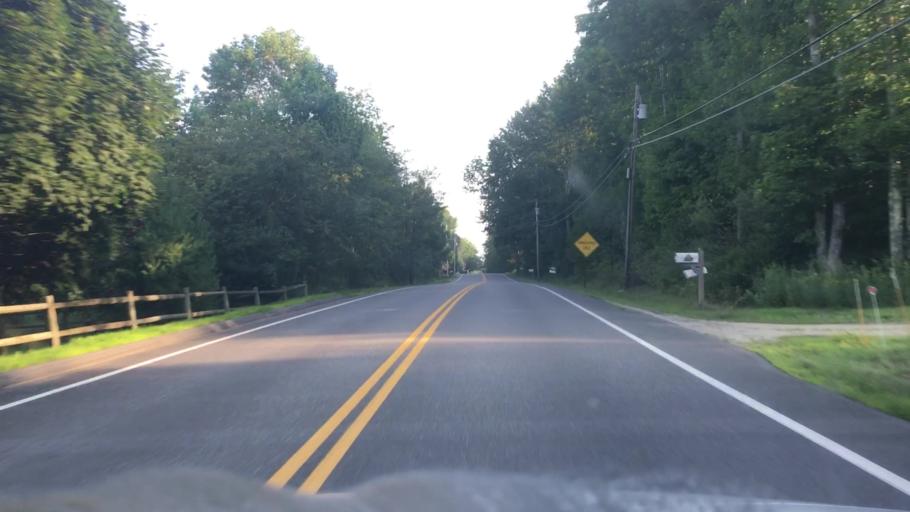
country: US
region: Maine
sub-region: Cumberland County
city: Freeport
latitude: 43.9143
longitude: -70.0906
